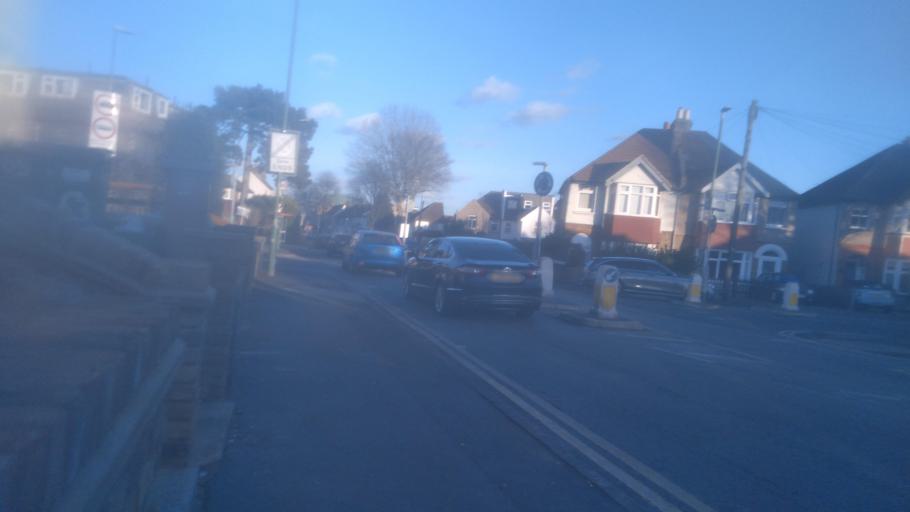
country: GB
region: England
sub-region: Greater London
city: Carshalton
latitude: 51.3657
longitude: -0.1830
